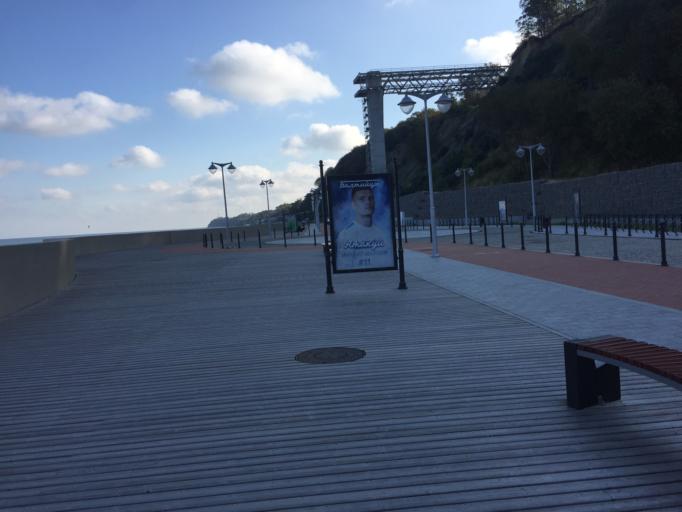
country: RU
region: Kaliningrad
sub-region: Gorod Svetlogorsk
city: Svetlogorsk
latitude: 54.9470
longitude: 20.1569
